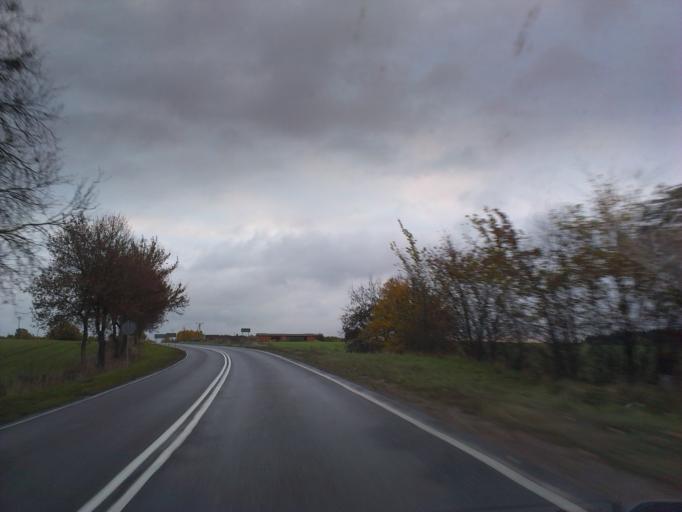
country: PL
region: Kujawsko-Pomorskie
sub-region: Powiat tucholski
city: Cekcyn
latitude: 53.5171
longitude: 17.9548
